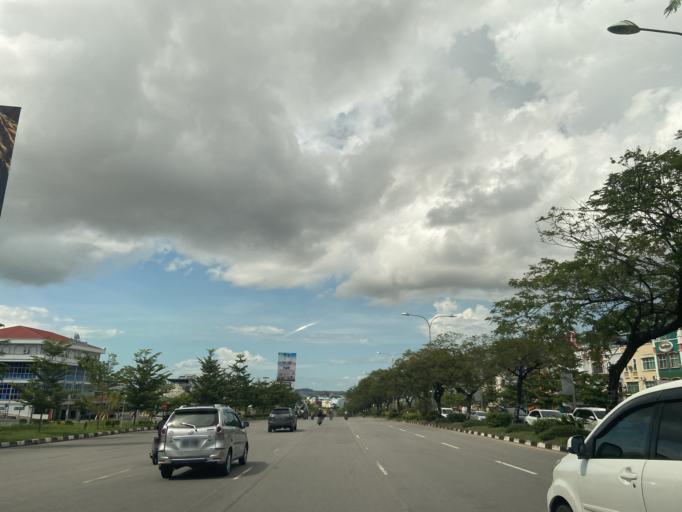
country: SG
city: Singapore
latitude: 1.1267
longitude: 104.0322
